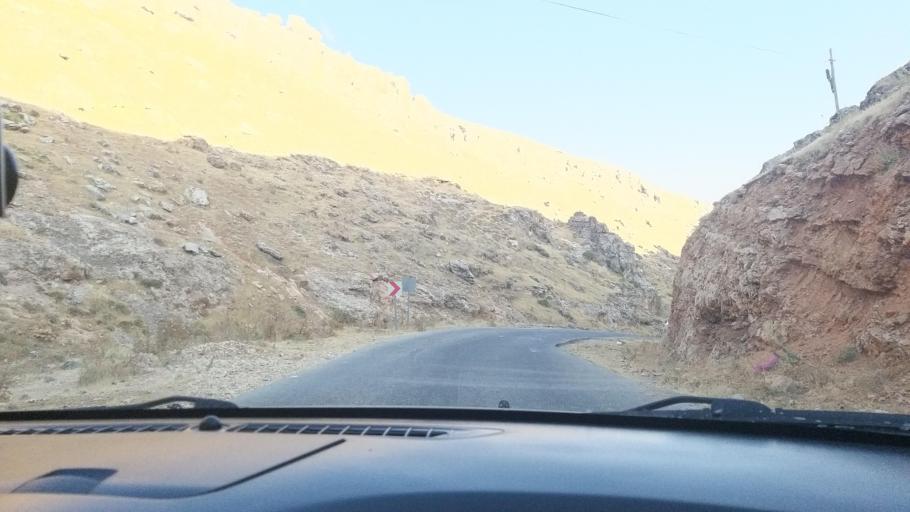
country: TR
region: Diyarbakir
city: Silvan
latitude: 38.1634
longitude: 41.0014
